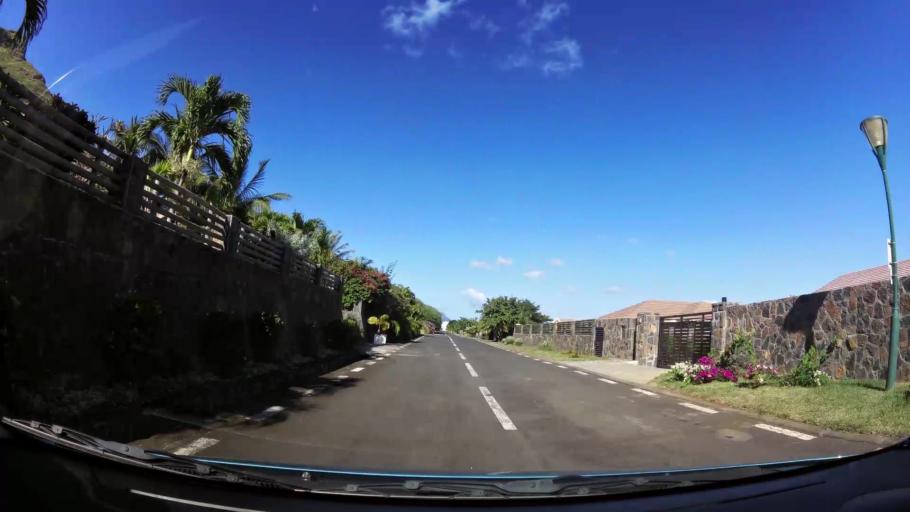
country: MU
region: Black River
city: Tamarin
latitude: -20.3405
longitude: 57.3679
